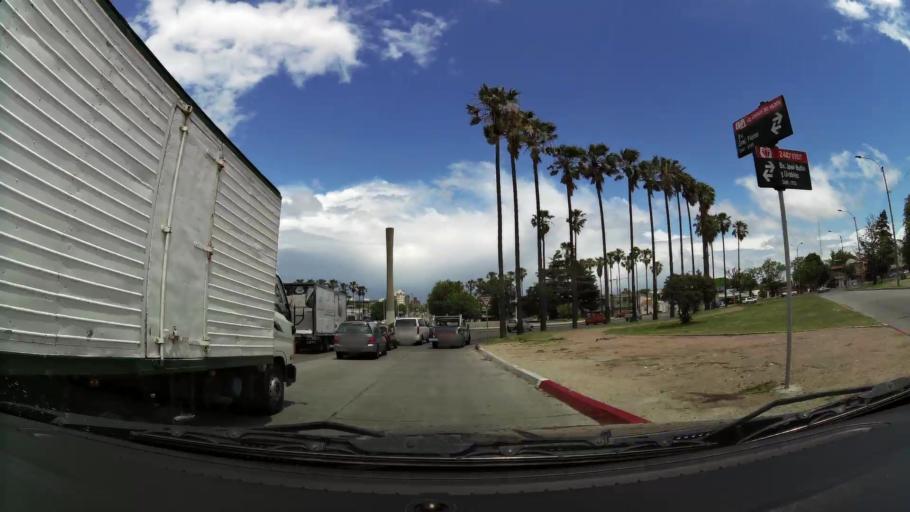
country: UY
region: Montevideo
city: Montevideo
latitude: -34.8623
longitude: -56.1686
